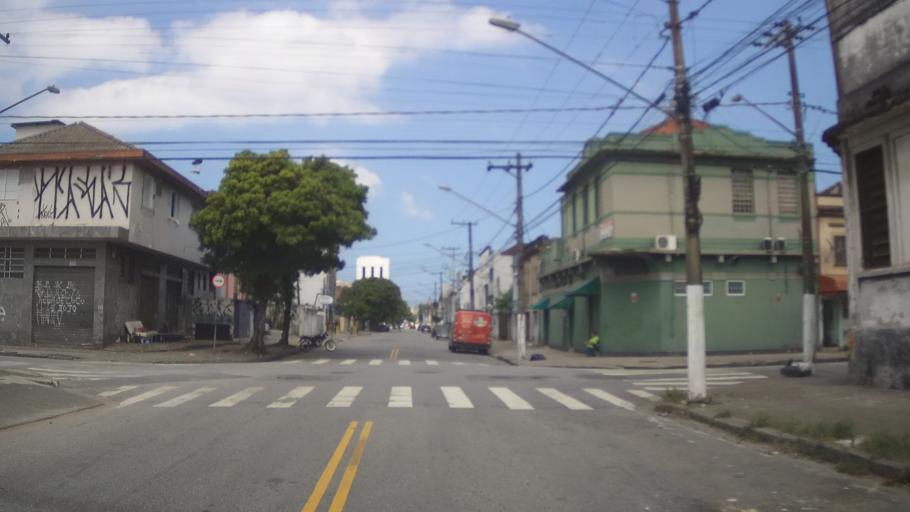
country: BR
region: Sao Paulo
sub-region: Santos
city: Santos
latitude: -23.9534
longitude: -46.3184
